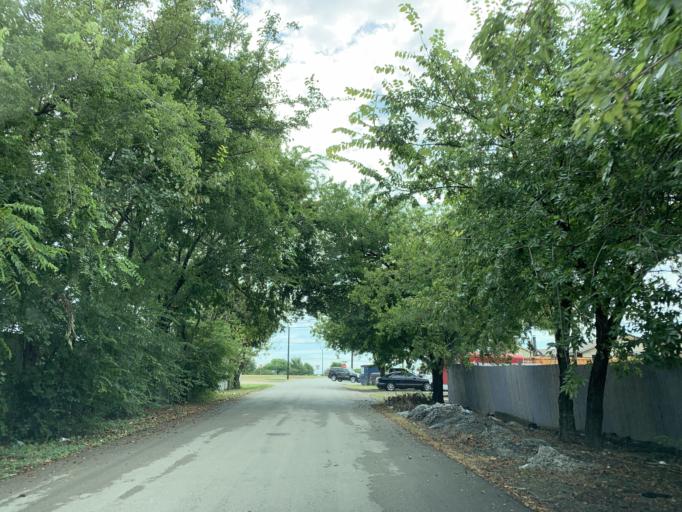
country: US
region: Texas
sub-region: Dallas County
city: Duncanville
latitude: 32.6724
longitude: -96.8242
